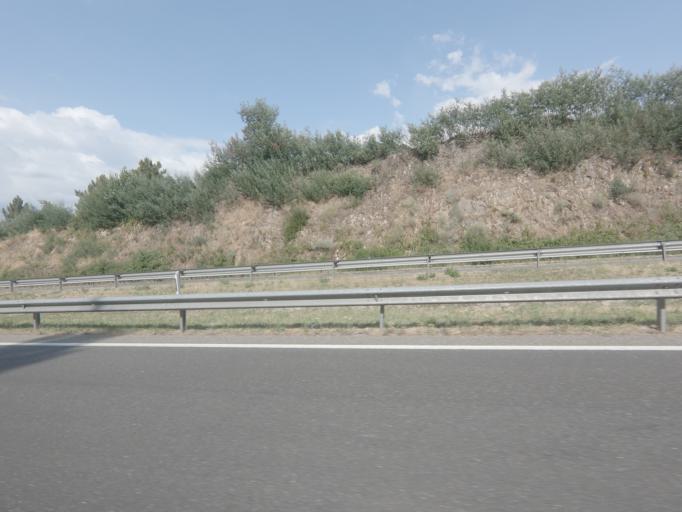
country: ES
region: Galicia
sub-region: Provincia de Ourense
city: Ourense
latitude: 42.3252
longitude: -7.8877
